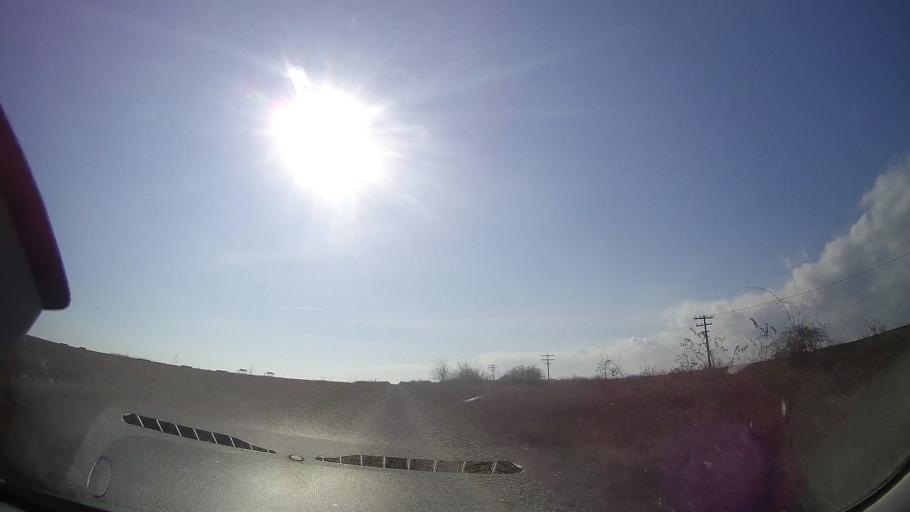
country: RO
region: Constanta
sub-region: Comuna Costinesti
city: Schitu
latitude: 43.9201
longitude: 28.6300
